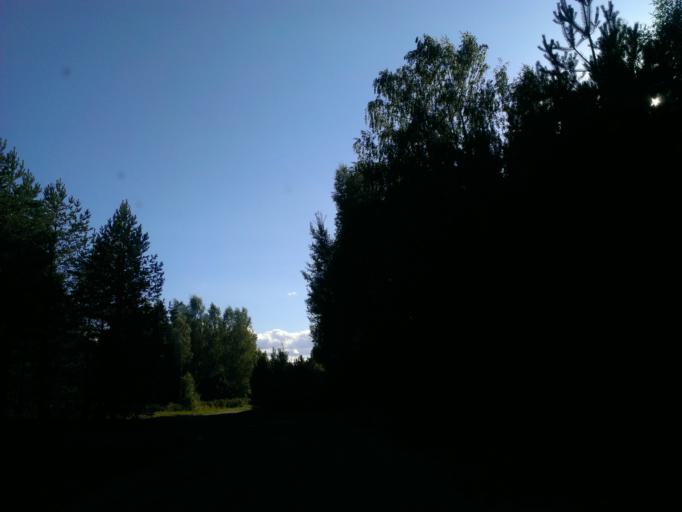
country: LV
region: Adazi
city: Adazi
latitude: 57.0596
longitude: 24.2595
